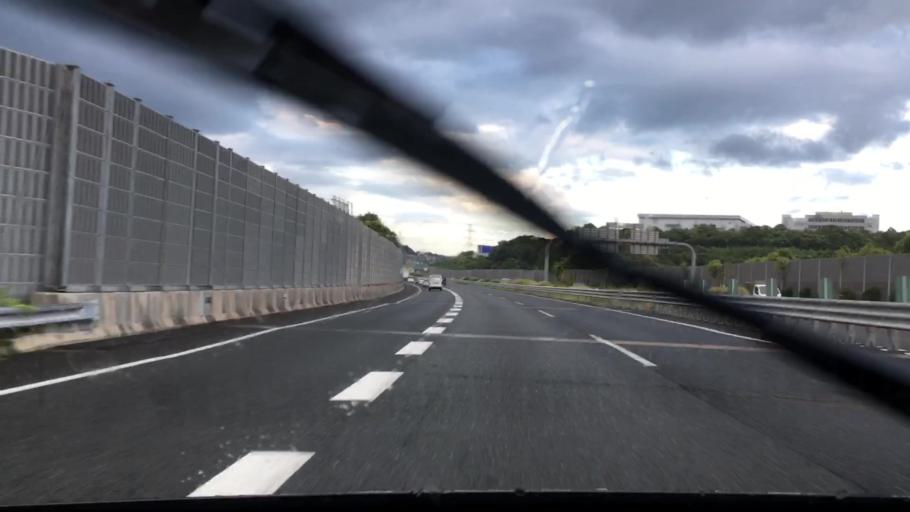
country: JP
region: Fukuoka
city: Kitakyushu
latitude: 33.8262
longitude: 130.8967
